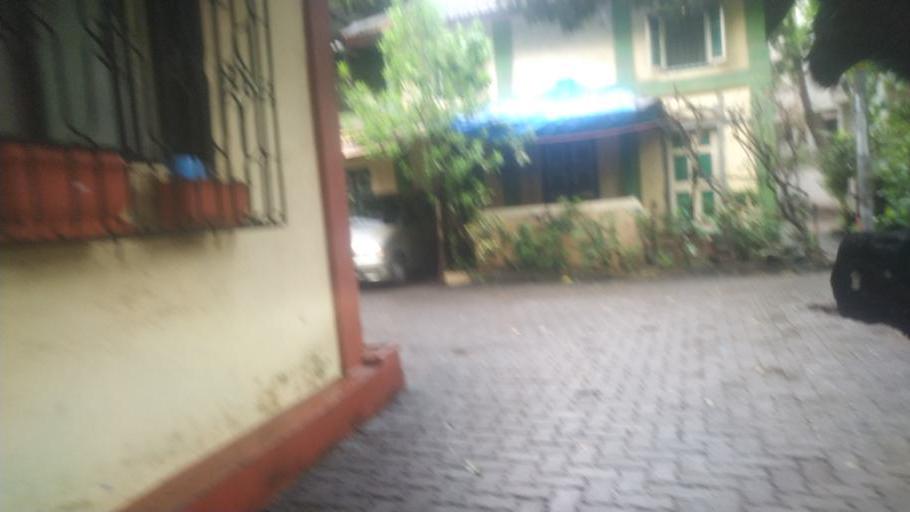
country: IN
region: Maharashtra
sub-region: Mumbai Suburban
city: Powai
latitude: 19.1190
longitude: 72.8540
